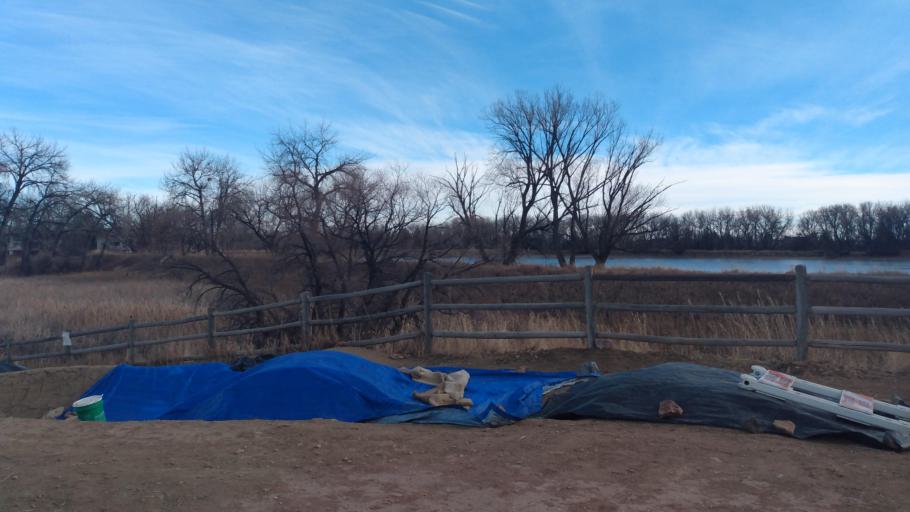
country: US
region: Colorado
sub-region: Boulder County
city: Gunbarrel
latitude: 40.0638
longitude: -105.1998
